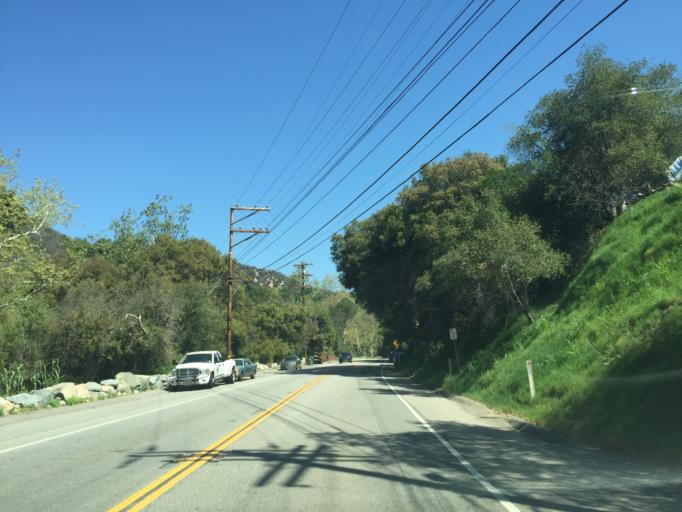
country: US
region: California
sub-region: Los Angeles County
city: Topanga
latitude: 34.0982
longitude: -118.5996
